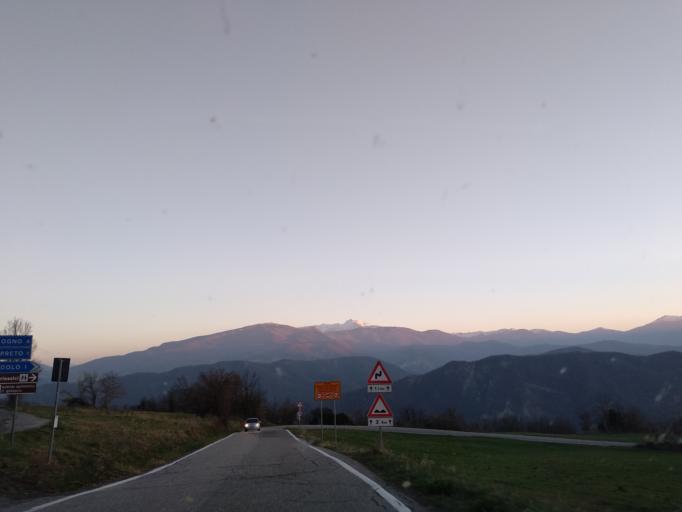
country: IT
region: Emilia-Romagna
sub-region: Provincia di Reggio Emilia
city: Castelnovo ne'Monti
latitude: 44.4123
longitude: 10.4023
